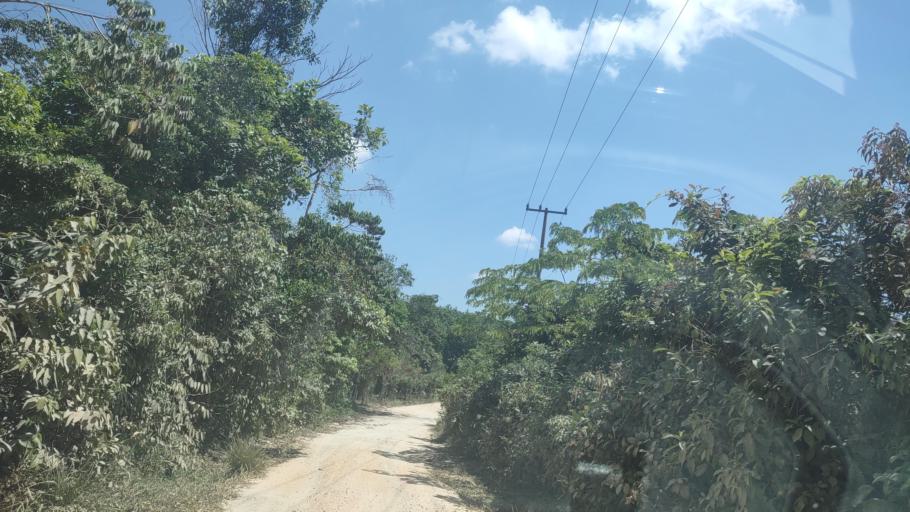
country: MX
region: Veracruz
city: Las Choapas
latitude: 17.7798
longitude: -94.1410
